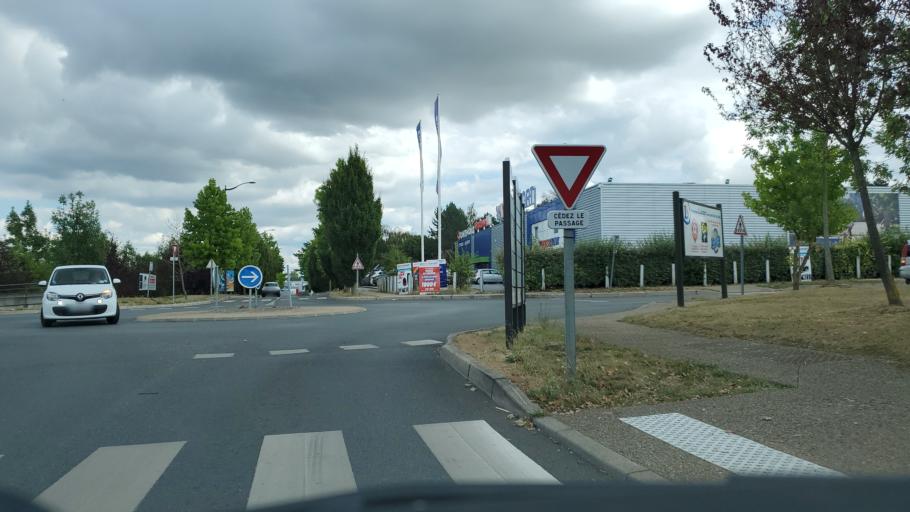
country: FR
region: Ile-de-France
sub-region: Departement de Seine-et-Marne
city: Villenoy
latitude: 48.9366
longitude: 2.8766
